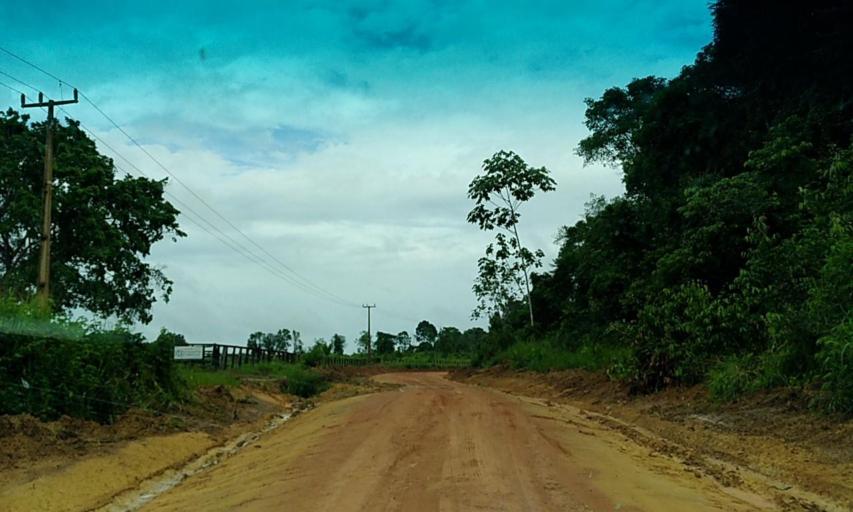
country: BR
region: Para
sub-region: Senador Jose Porfirio
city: Senador Jose Porfirio
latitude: -3.0120
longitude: -51.6812
